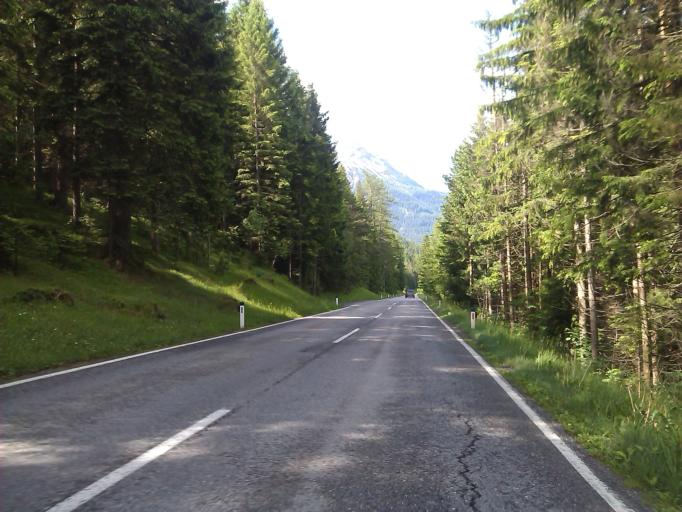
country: AT
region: Tyrol
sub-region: Politischer Bezirk Reutte
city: Ehrwald
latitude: 47.3887
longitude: 10.9119
